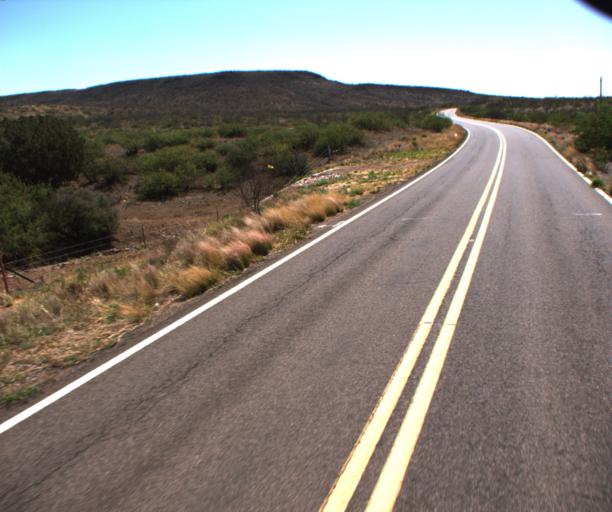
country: US
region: Arizona
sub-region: Cochise County
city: Douglas
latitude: 31.4742
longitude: -109.3937
